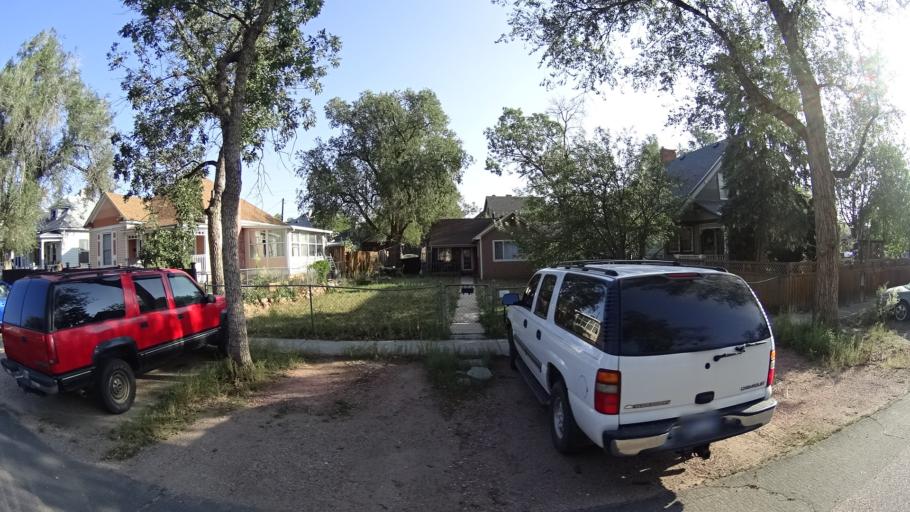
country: US
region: Colorado
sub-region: El Paso County
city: Colorado Springs
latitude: 38.8318
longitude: -104.8383
